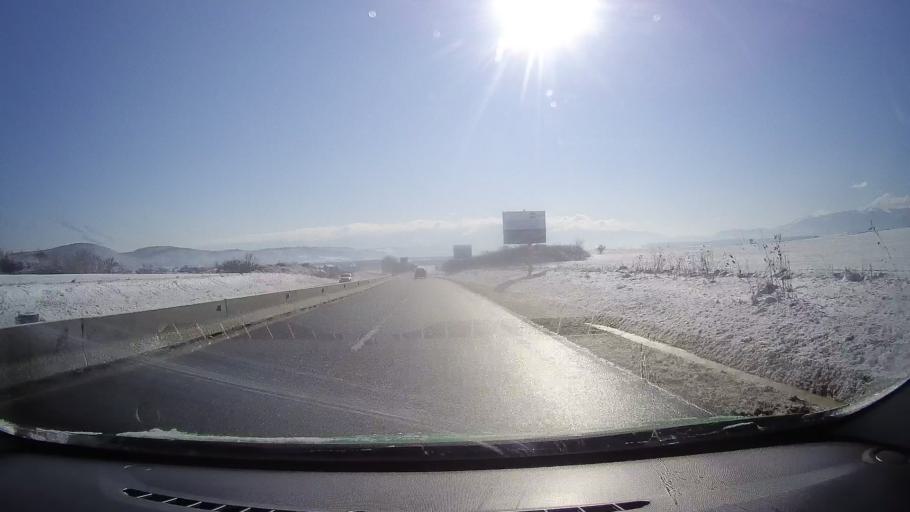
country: RO
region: Sibiu
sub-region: Comuna Selimbar
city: Selimbar
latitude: 45.7614
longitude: 24.1929
